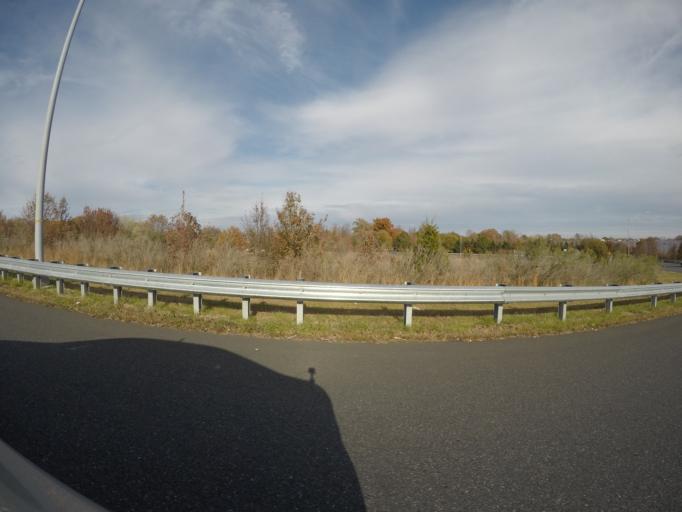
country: US
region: Maryland
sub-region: Harford County
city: Riverside
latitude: 39.4697
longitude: -76.2321
